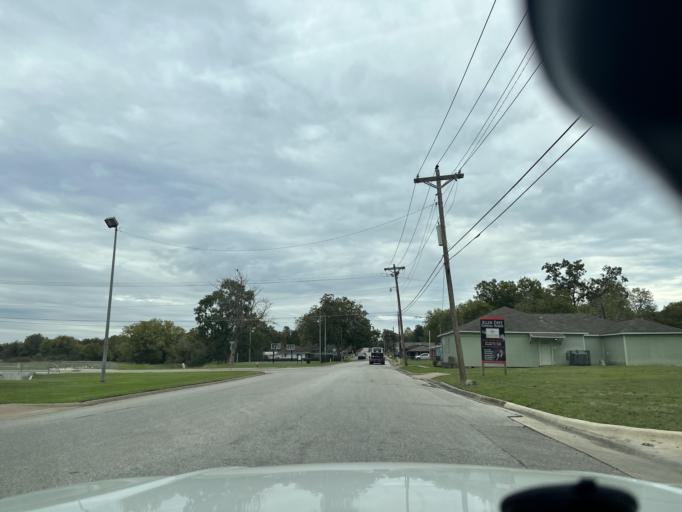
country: US
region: Texas
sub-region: Washington County
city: Brenham
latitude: 30.1688
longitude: -96.4066
